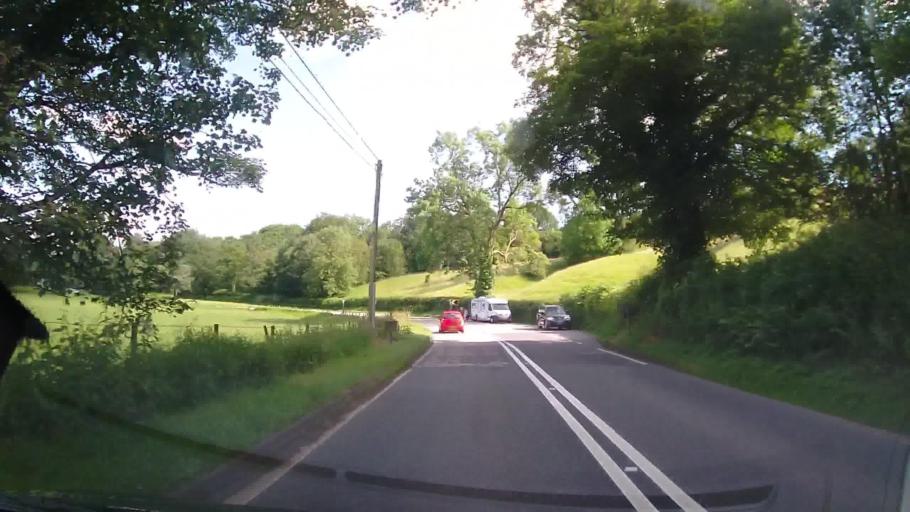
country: GB
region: Wales
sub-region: Sir Powys
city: Llanfyllin
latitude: 52.6603
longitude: -3.3623
